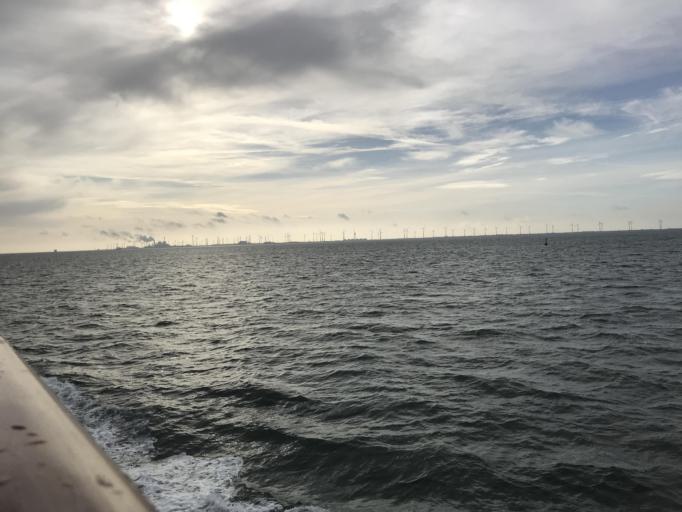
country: DE
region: Lower Saxony
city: Borkum
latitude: 53.5223
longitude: 6.7737
